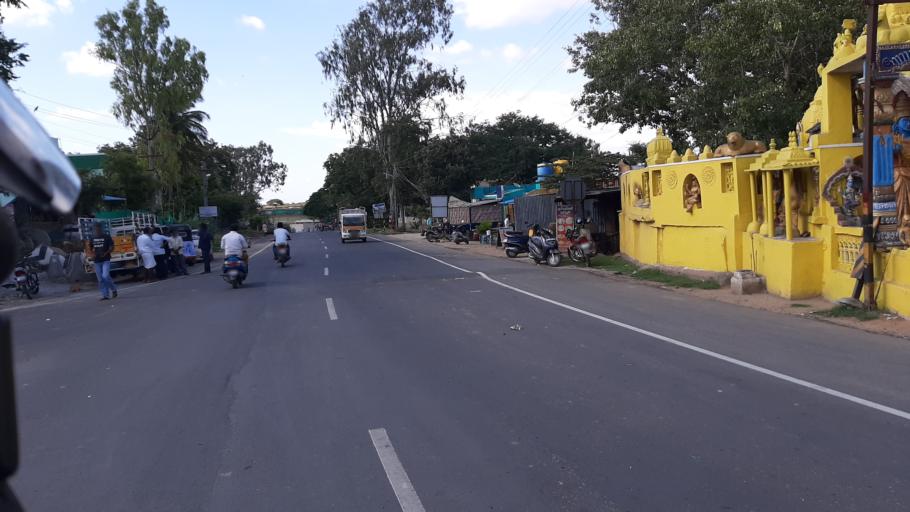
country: IN
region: Tamil Nadu
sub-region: Krishnagiri
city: Denkanikota
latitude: 12.5323
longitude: 77.7884
